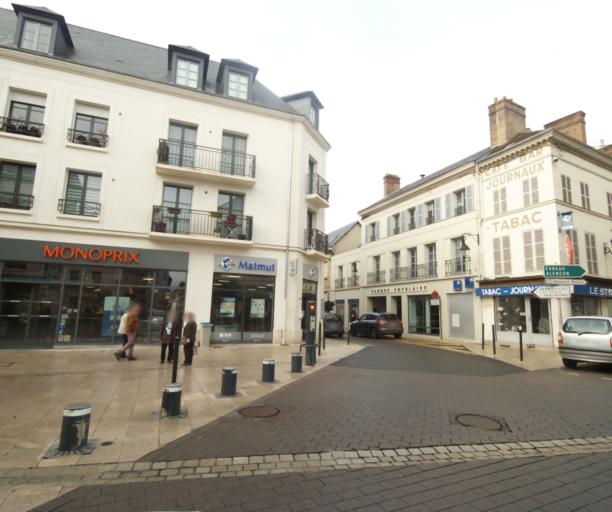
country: FR
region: Centre
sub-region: Departement d'Eure-et-Loir
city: Dreux
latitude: 48.7369
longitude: 1.3654
